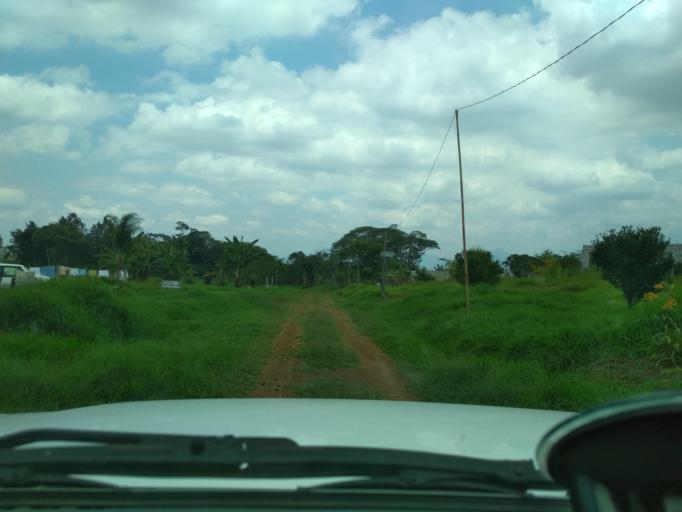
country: MX
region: Veracruz
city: Tocuila
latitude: 18.9470
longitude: -97.0156
